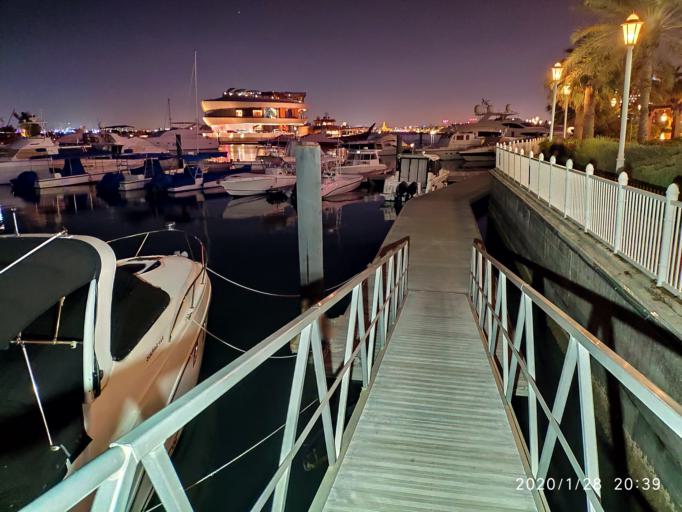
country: QA
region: Baladiyat ad Dawhah
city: Doha
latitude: 25.3252
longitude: 51.5408
